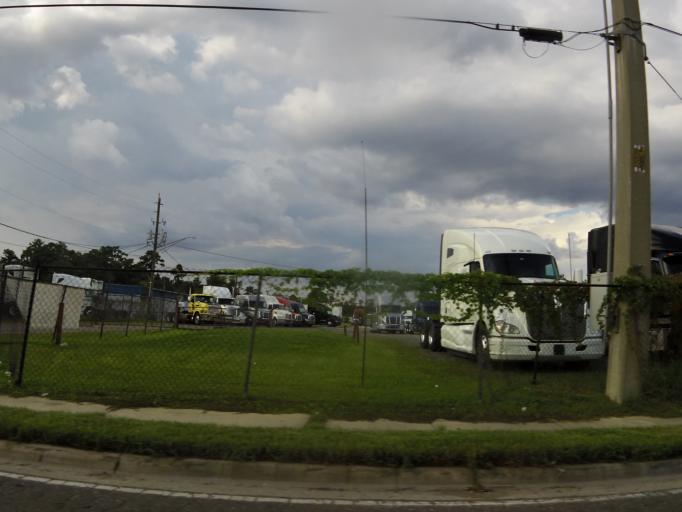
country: US
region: Florida
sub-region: Duval County
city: Jacksonville
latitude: 30.3358
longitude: -81.7496
